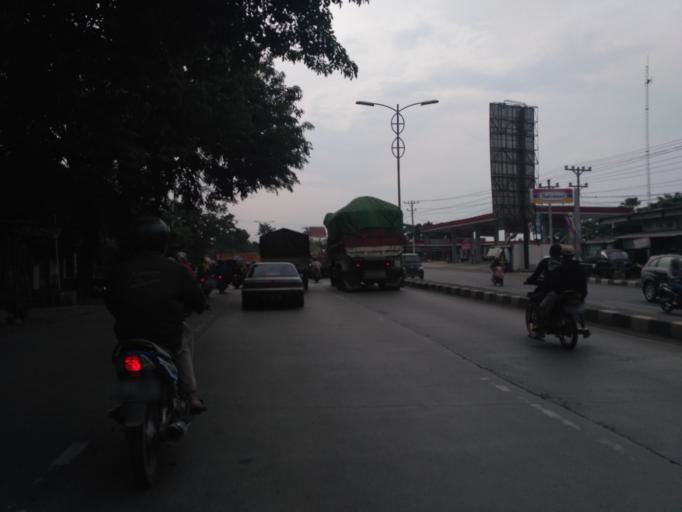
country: ID
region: Central Java
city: Semarang
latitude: -6.9738
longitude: 110.3143
